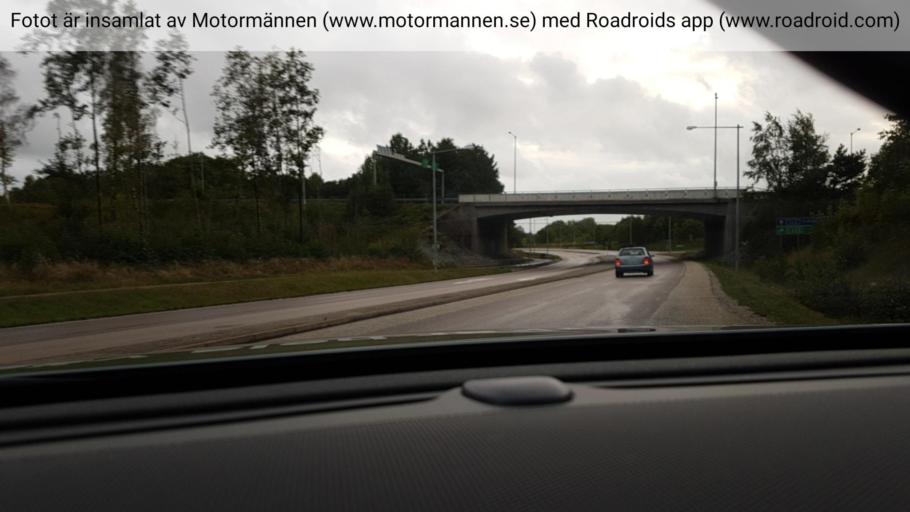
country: SE
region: Vaestra Goetaland
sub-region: Stenungsunds Kommun
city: Stenungsund
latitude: 58.0595
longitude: 11.8760
